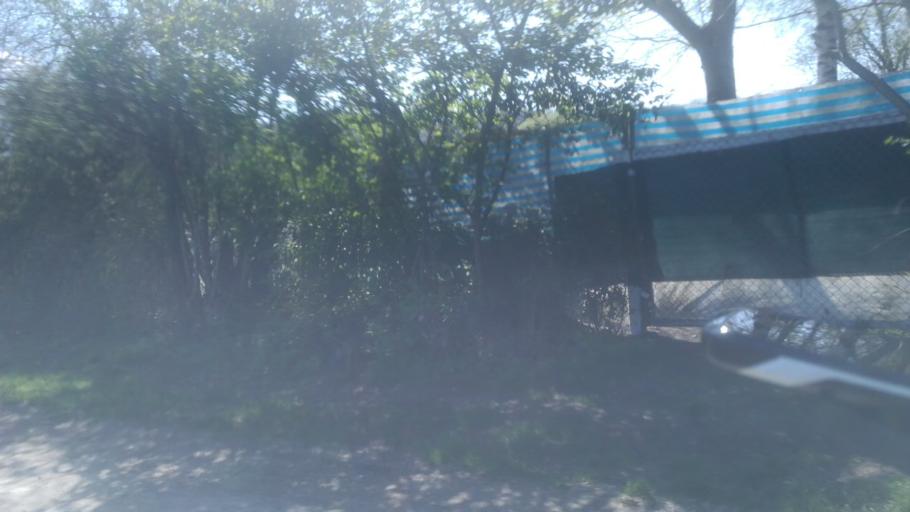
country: DE
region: Baden-Wuerttemberg
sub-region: Freiburg Region
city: Singen
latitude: 47.7806
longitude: 8.8521
